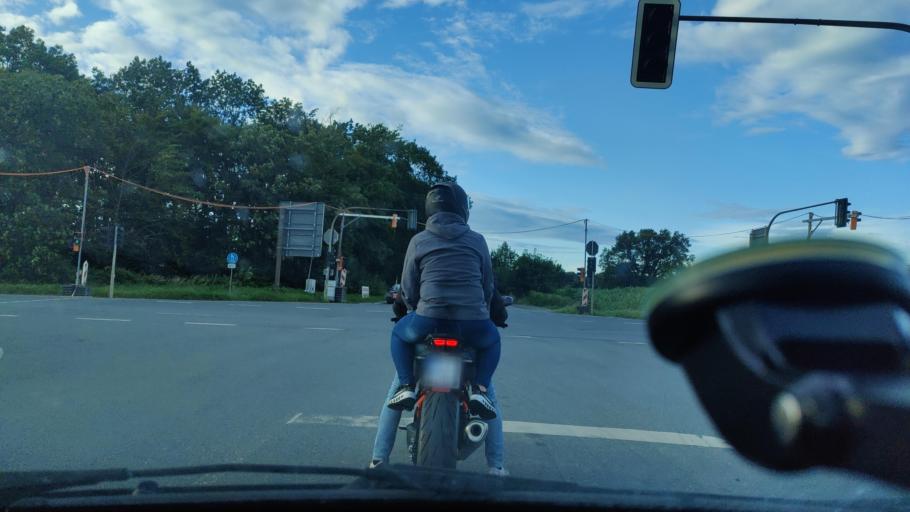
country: DE
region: North Rhine-Westphalia
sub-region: Regierungsbezirk Dusseldorf
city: Schermbeck
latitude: 51.6131
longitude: 6.8918
